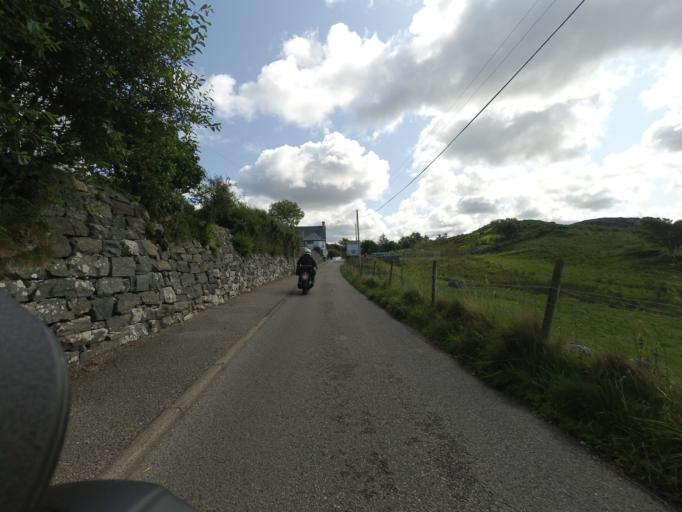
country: GB
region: Scotland
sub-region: Highland
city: Ullapool
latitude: 58.2436
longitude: -5.2032
